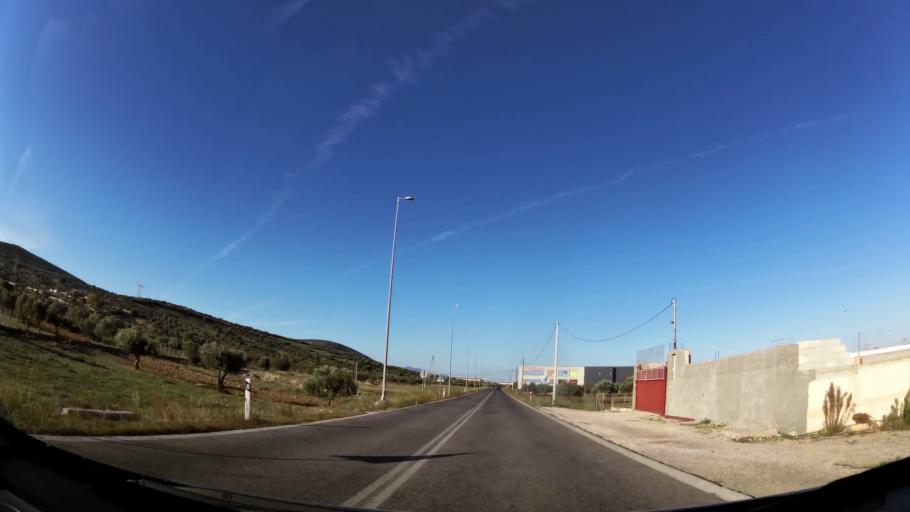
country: GR
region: Attica
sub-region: Nomarchia Anatolikis Attikis
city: Kalyvia Thorikou
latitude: 37.8529
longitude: 23.9182
